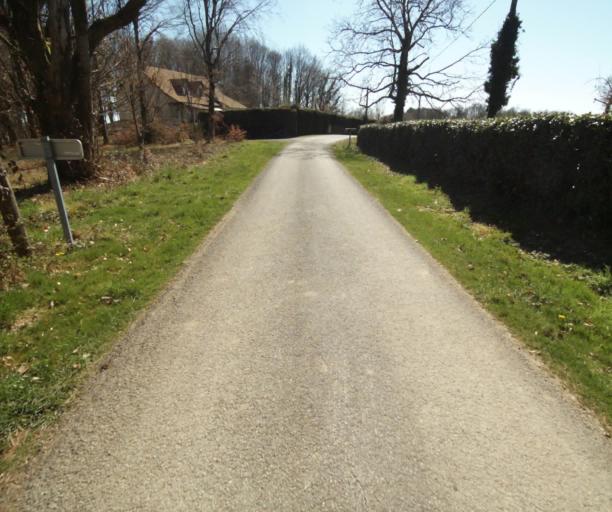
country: FR
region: Limousin
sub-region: Departement de la Correze
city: Uzerche
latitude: 45.3882
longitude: 1.6067
